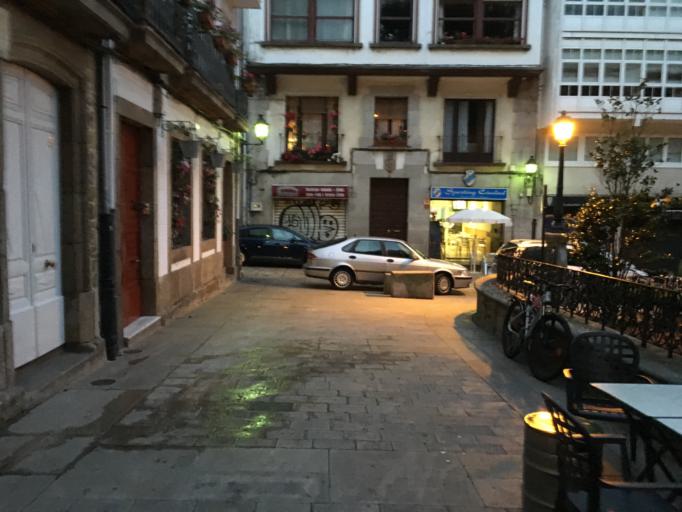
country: ES
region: Galicia
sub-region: Provincia da Coruna
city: A Coruna
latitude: 43.3701
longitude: -8.3932
